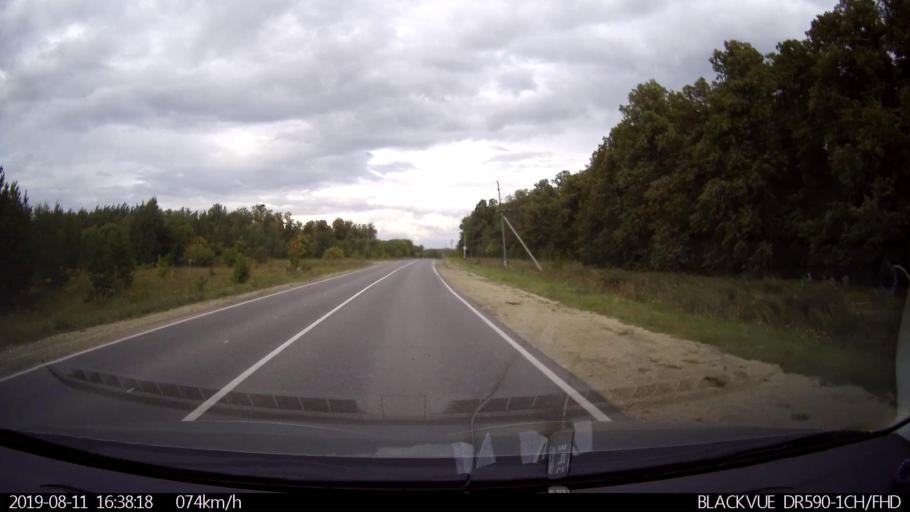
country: RU
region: Ulyanovsk
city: Mayna
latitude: 54.1341
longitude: 47.6236
